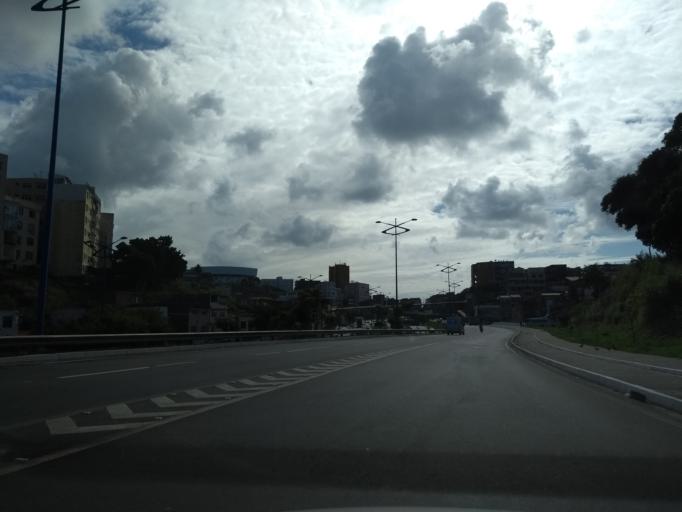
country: BR
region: Bahia
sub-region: Salvador
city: Salvador
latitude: -12.9622
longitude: -38.4960
